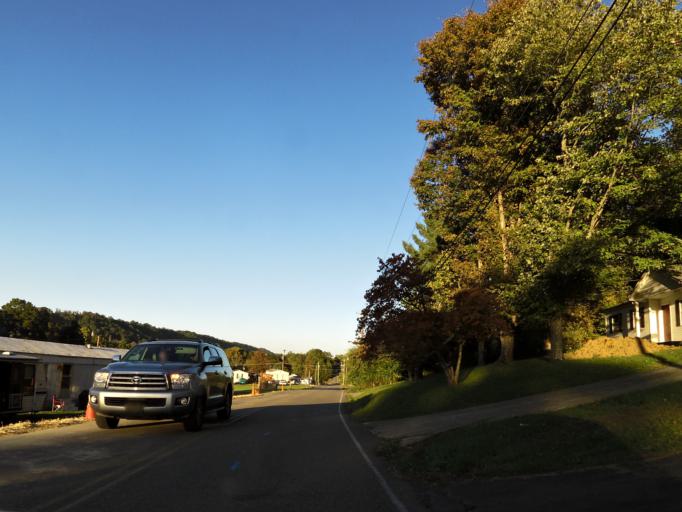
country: US
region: Tennessee
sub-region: Knox County
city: Knoxville
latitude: 36.0554
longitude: -83.9304
